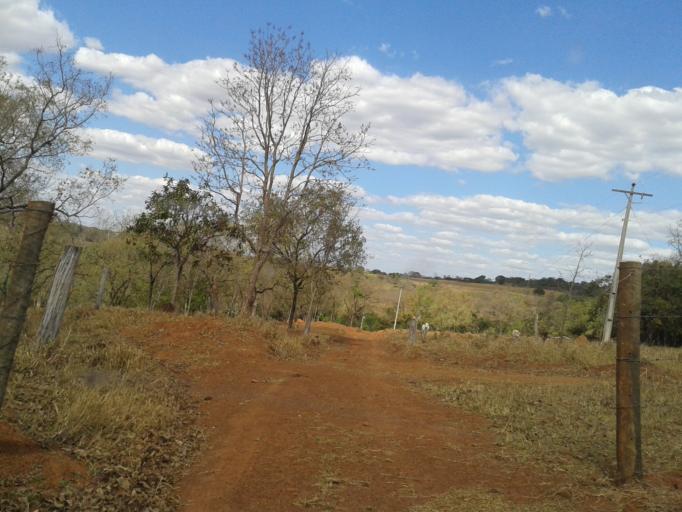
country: BR
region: Minas Gerais
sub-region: Monte Alegre De Minas
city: Monte Alegre de Minas
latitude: -18.7901
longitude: -49.0958
